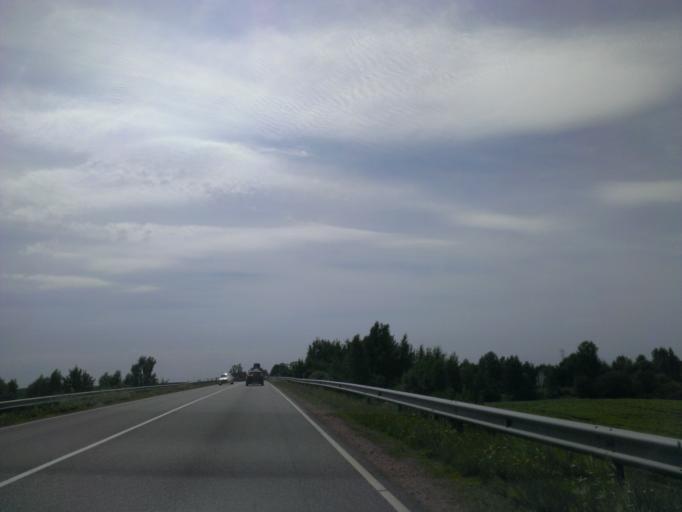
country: LV
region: Salaspils
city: Salaspils
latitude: 56.8546
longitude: 24.4011
